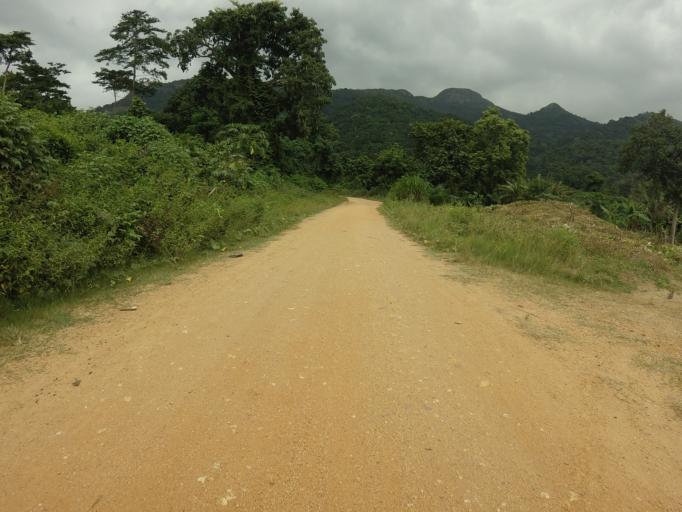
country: GH
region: Volta
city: Kpandu
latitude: 6.8732
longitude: 0.4236
